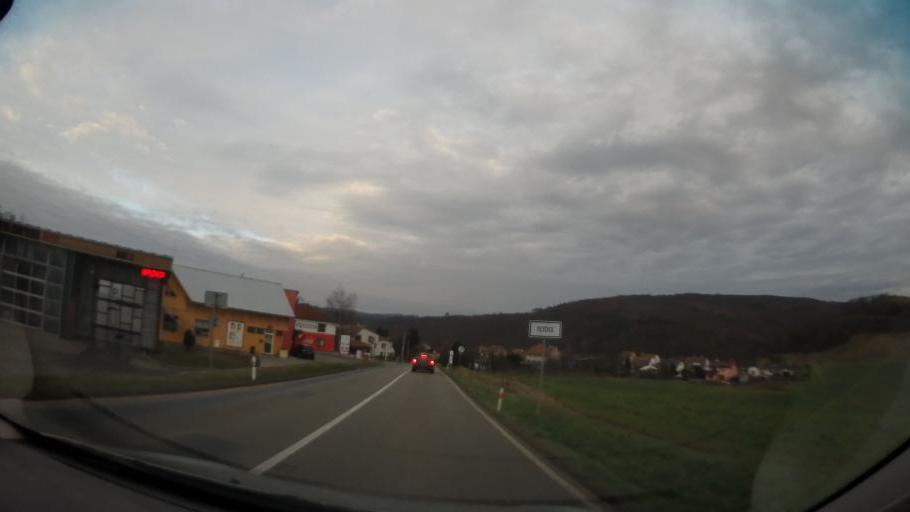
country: CZ
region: South Moravian
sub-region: Okres Brno-Venkov
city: Rosice
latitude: 49.1651
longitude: 16.3959
